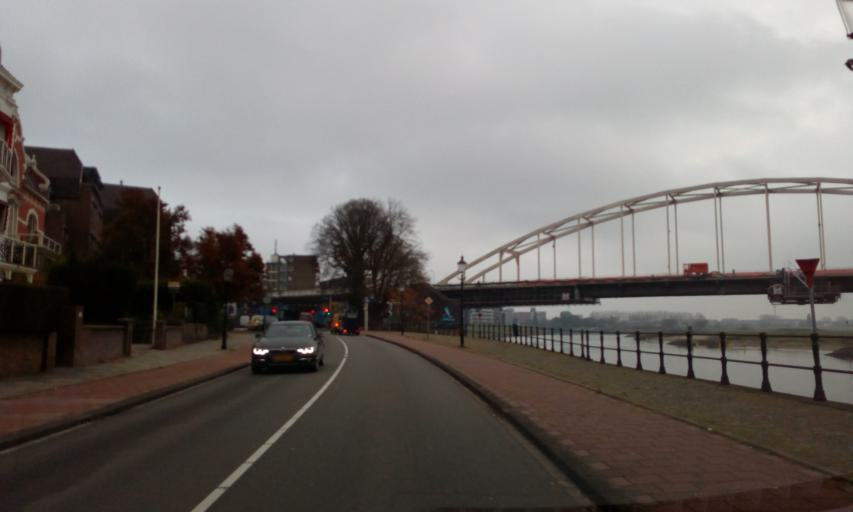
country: NL
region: Overijssel
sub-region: Gemeente Deventer
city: Deventer
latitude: 52.2502
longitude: 6.1567
